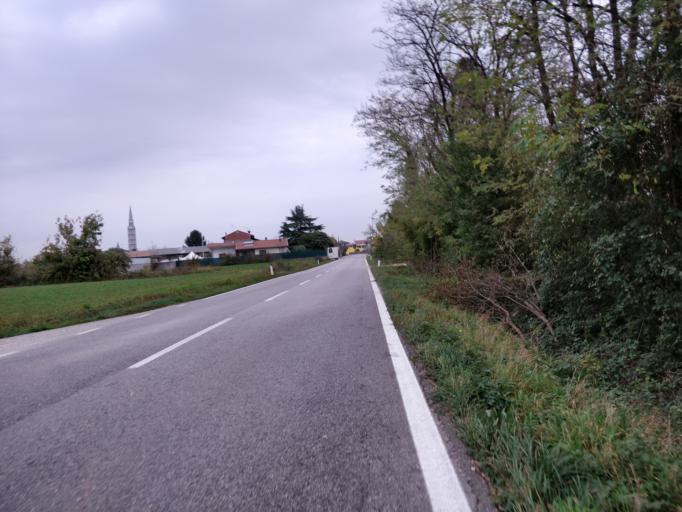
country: IT
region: Friuli Venezia Giulia
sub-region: Provincia di Udine
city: Mortegliano
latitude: 45.9409
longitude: 13.1592
